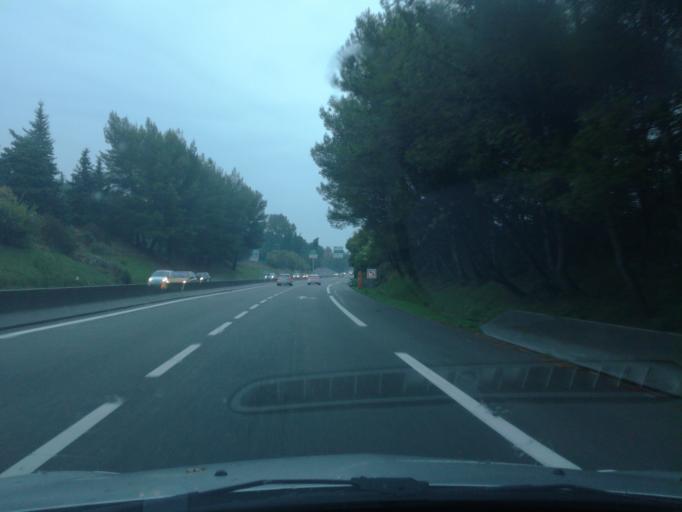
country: FR
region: Provence-Alpes-Cote d'Azur
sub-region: Departement des Alpes-Maritimes
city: Mougins
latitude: 43.5954
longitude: 7.0002
